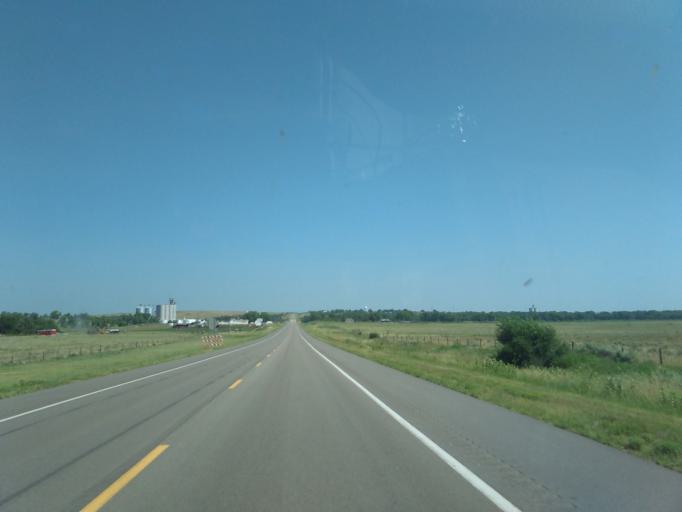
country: US
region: Nebraska
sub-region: Dundy County
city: Benkelman
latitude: 40.0267
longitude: -101.5429
